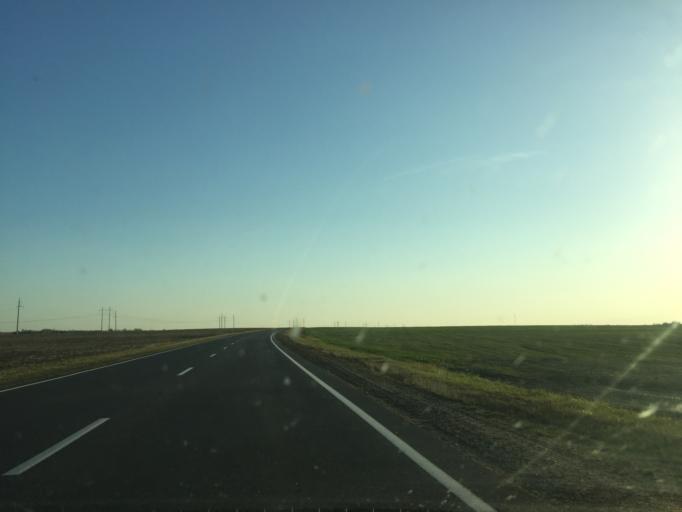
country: BY
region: Mogilev
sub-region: Mahilyowski Rayon
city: Kadino
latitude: 53.8363
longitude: 30.4796
